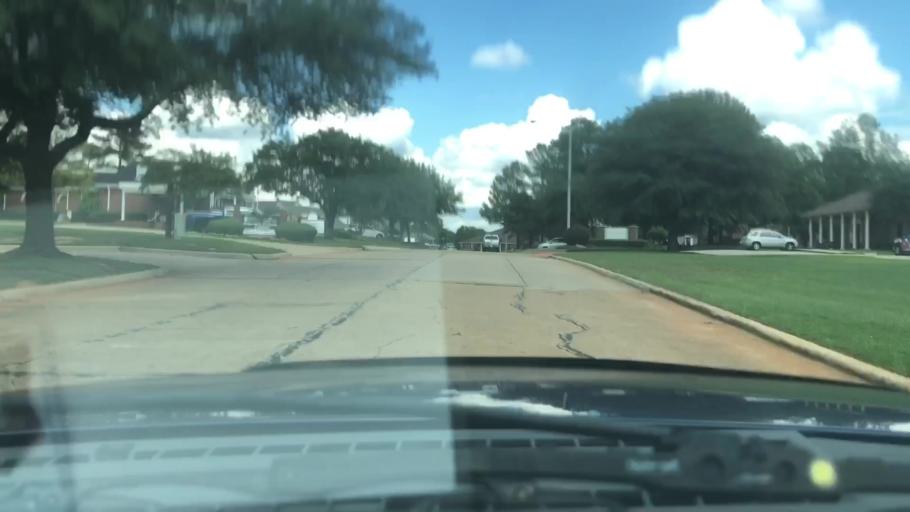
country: US
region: Arkansas
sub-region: Miller County
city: Texarkana
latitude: 33.4700
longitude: -94.0654
